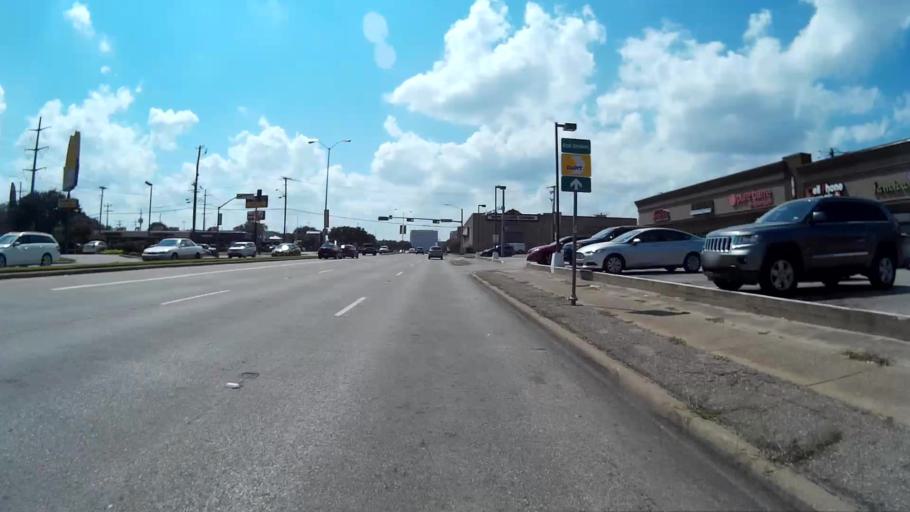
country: US
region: Texas
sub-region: Dallas County
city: University Park
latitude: 32.8578
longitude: -96.7686
